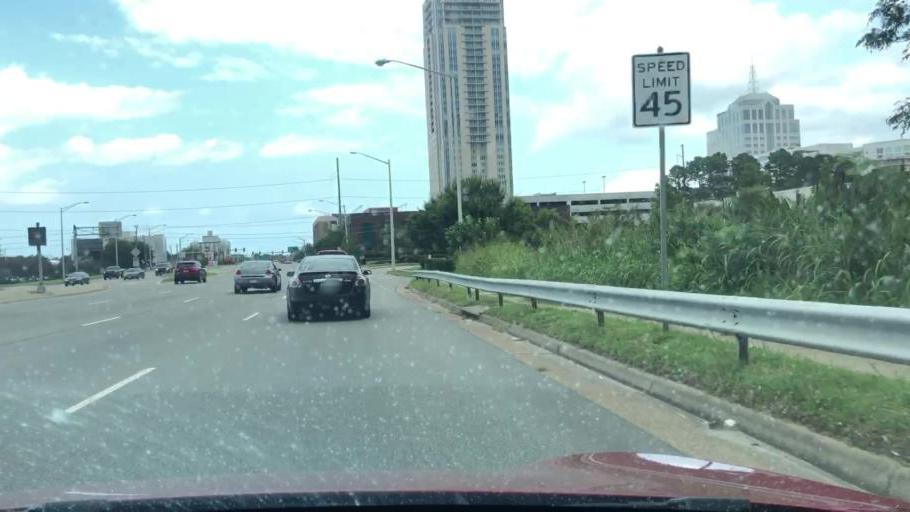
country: US
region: Virginia
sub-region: City of Chesapeake
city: Chesapeake
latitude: 36.8381
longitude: -76.1368
